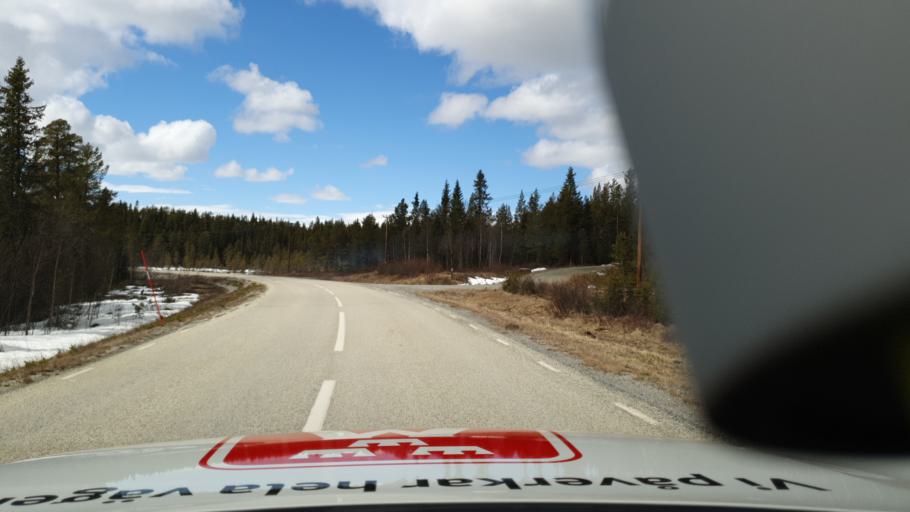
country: SE
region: Jaemtland
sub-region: Are Kommun
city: Are
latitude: 62.8086
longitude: 13.0254
